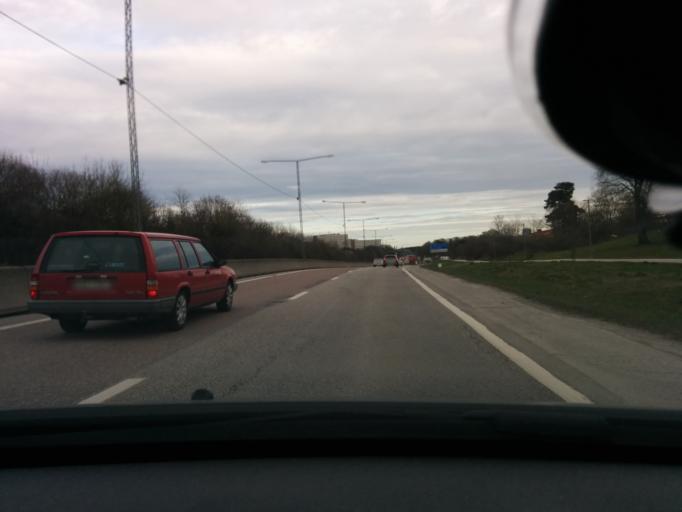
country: SE
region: Stockholm
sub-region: Jarfalla Kommun
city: Jakobsberg
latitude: 59.3611
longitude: 17.8679
